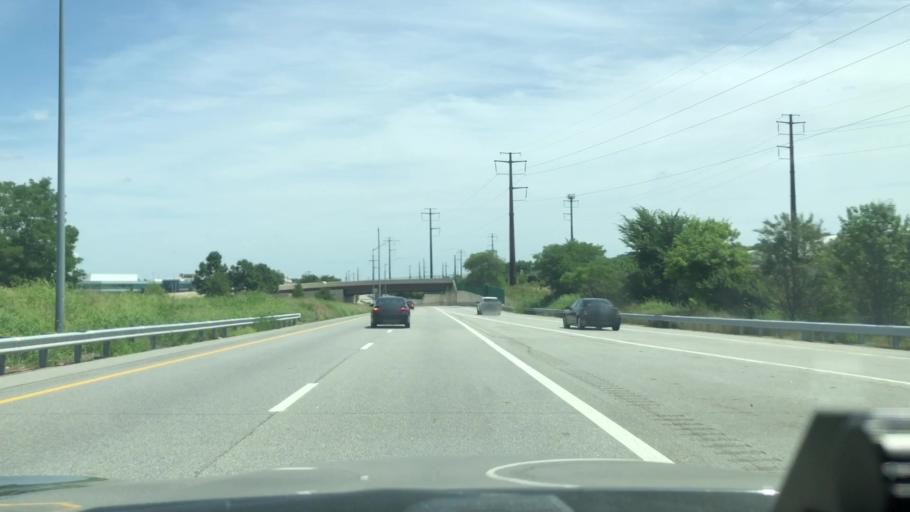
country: US
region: Pennsylvania
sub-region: Montgomery County
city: King of Prussia
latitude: 40.0780
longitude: -75.4081
